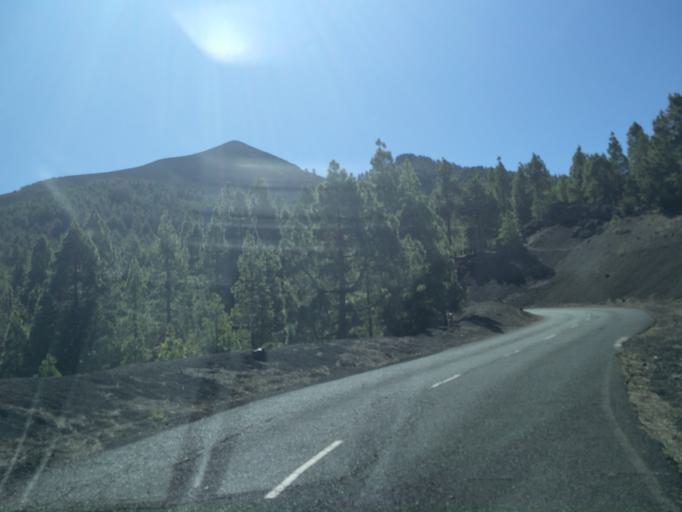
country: ES
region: Canary Islands
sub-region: Provincia de Santa Cruz de Tenerife
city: El Paso
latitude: 28.6175
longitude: -17.8460
